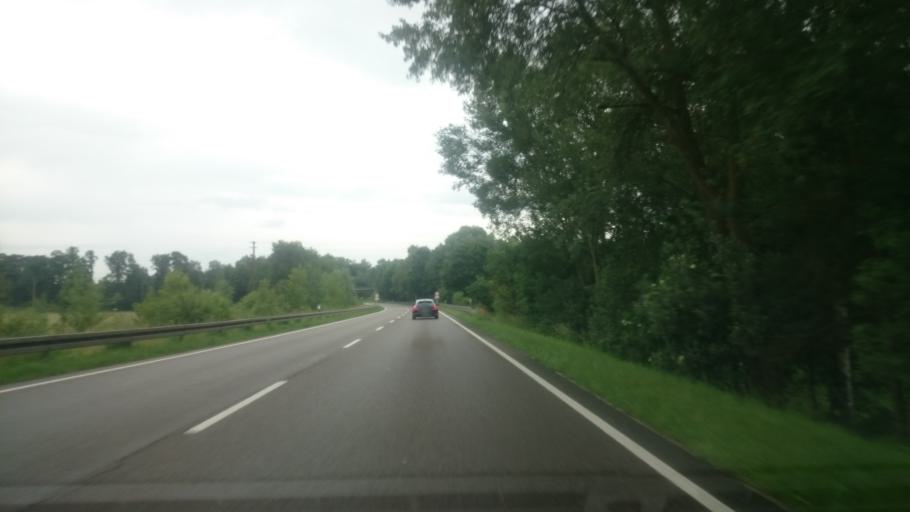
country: DE
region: Bavaria
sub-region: Upper Bavaria
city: Pornbach
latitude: 48.6098
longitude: 11.4342
